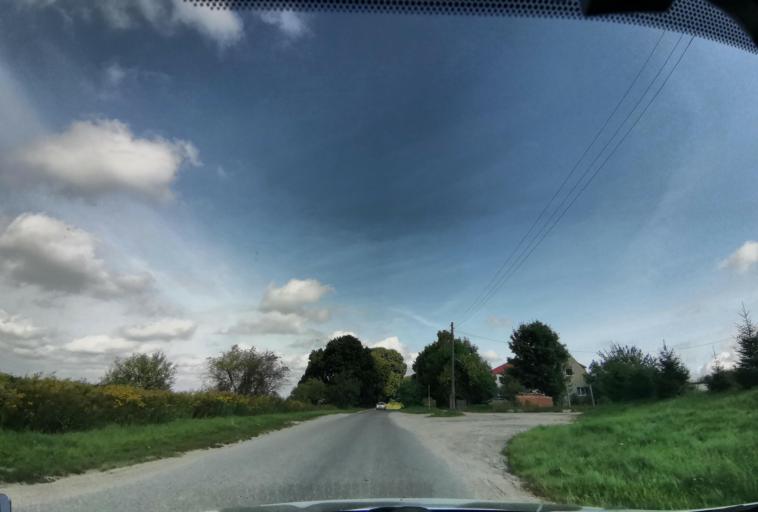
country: RU
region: Kaliningrad
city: Chernyakhovsk
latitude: 54.6513
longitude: 21.8154
